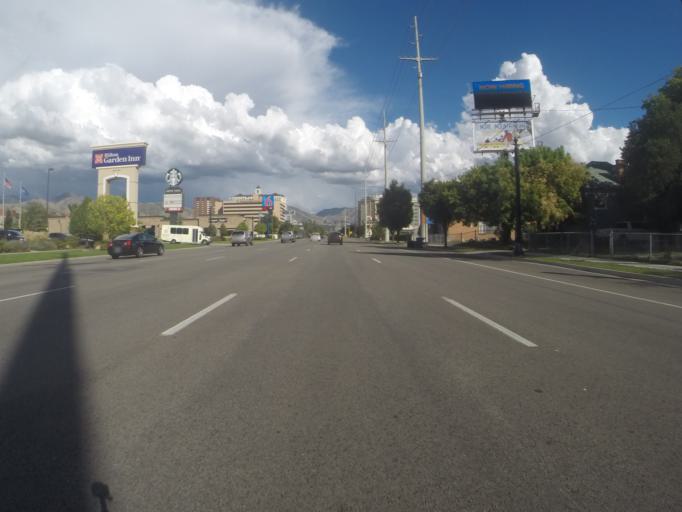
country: US
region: Utah
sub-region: Salt Lake County
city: Salt Lake City
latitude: 40.7563
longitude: -111.8987
